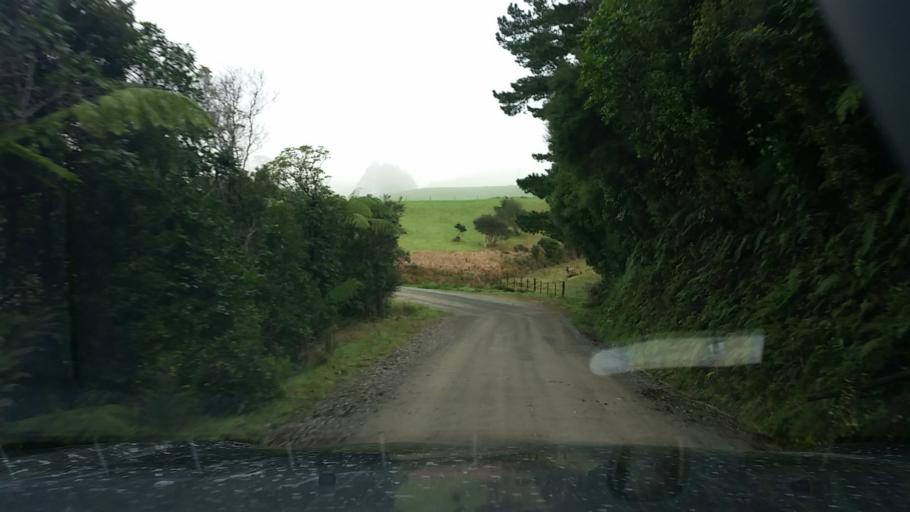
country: NZ
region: Marlborough
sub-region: Marlborough District
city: Picton
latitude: -41.1677
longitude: 174.0082
